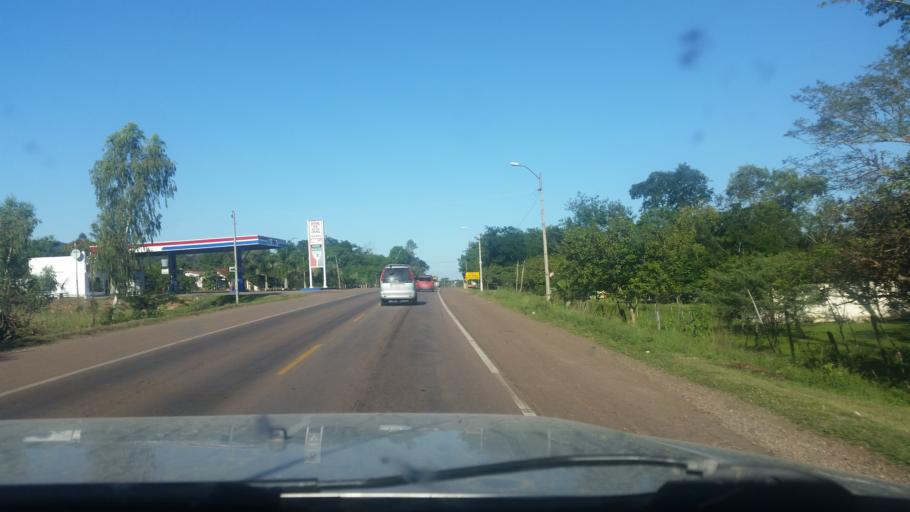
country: PY
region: Paraguari
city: Sapucai
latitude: -25.6648
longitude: -56.9623
